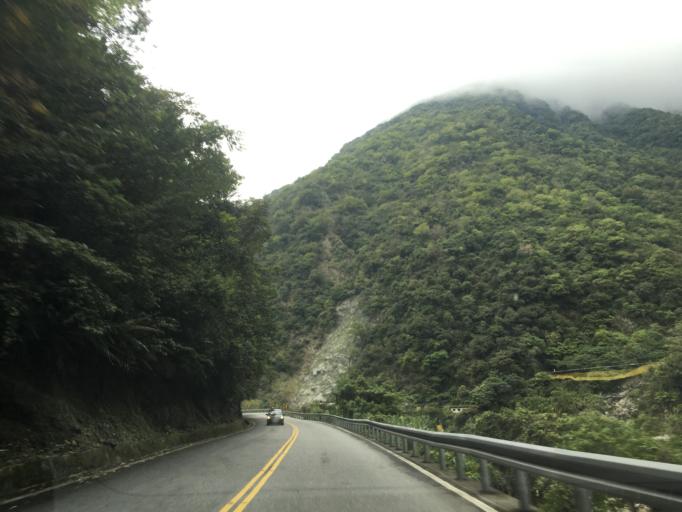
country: TW
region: Taiwan
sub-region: Hualien
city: Hualian
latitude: 24.1771
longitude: 121.5866
